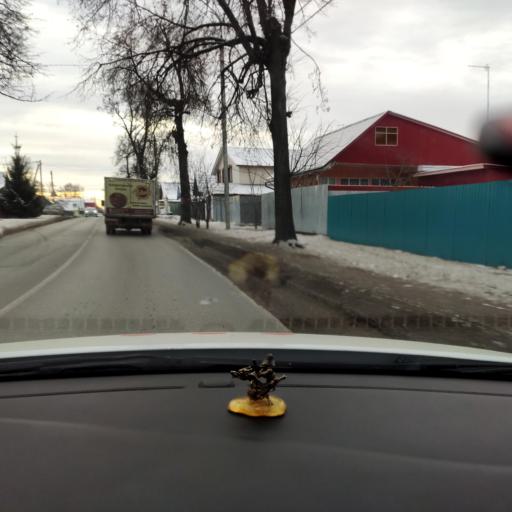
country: RU
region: Tatarstan
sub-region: Zelenodol'skiy Rayon
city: Zelenodolsk
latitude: 55.8594
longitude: 48.5329
